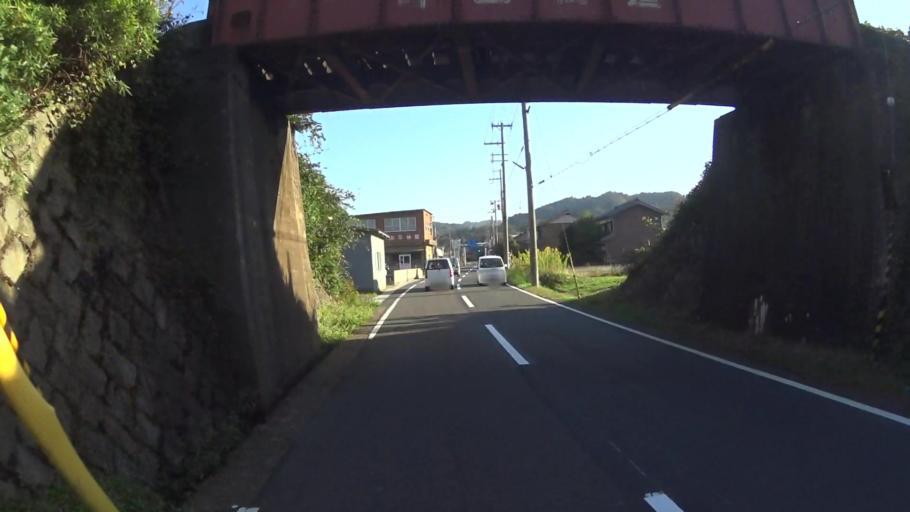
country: JP
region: Hyogo
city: Toyooka
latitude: 35.6048
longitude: 134.9016
